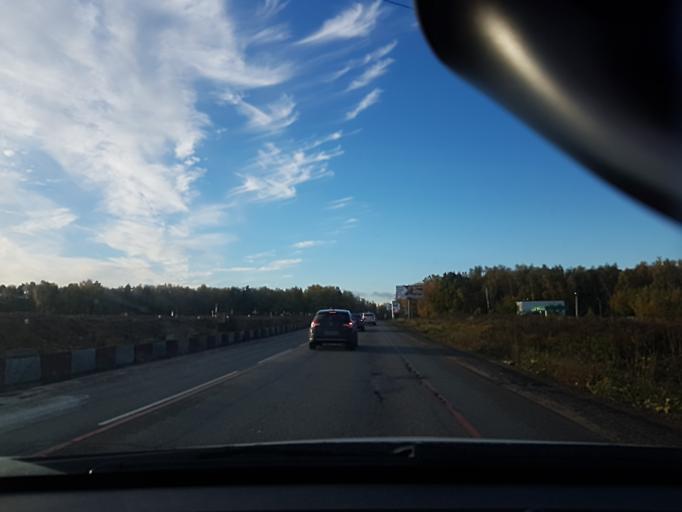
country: RU
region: Moskovskaya
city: Snegiri
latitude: 55.8657
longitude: 36.9404
